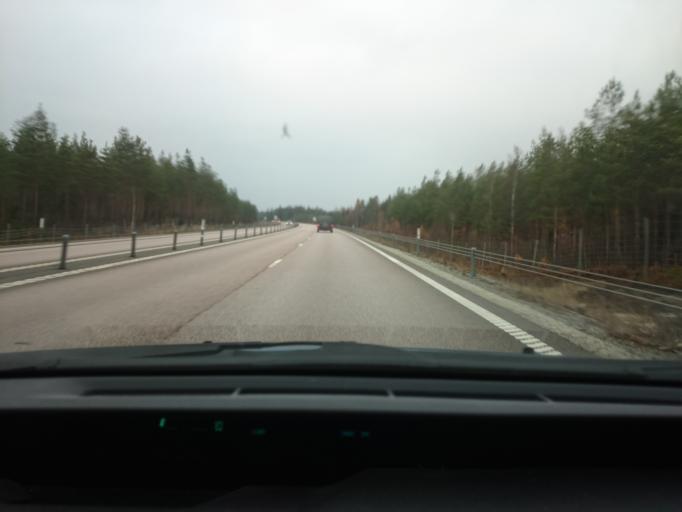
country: SE
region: Vaestmanland
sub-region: Sala Kommun
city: Sala
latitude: 59.9882
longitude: 16.4521
